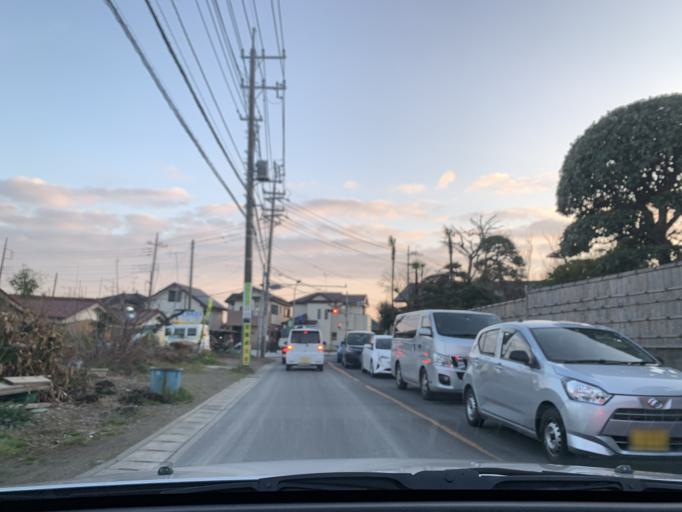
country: JP
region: Chiba
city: Matsudo
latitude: 35.7634
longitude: 139.9196
